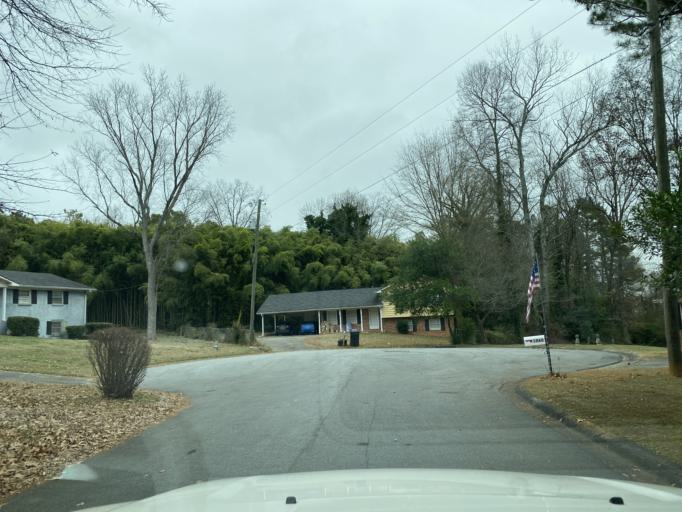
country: US
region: Georgia
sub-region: Cobb County
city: Fair Oaks
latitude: 33.9160
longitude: -84.5840
